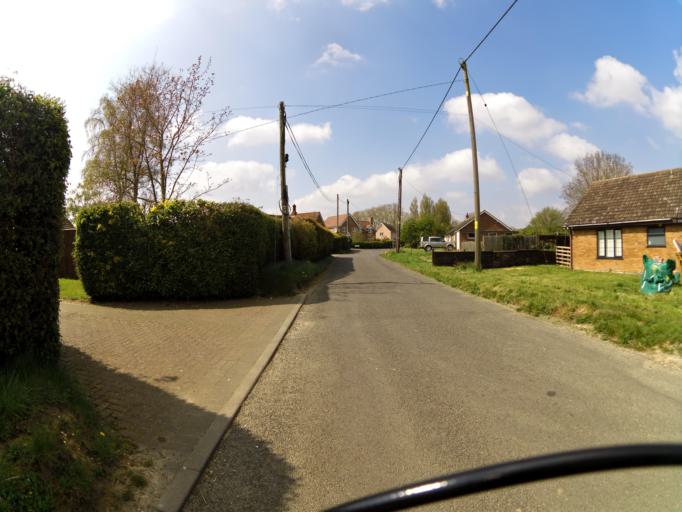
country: GB
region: England
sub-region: Suffolk
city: Hadleigh
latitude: 52.0799
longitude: 0.9894
